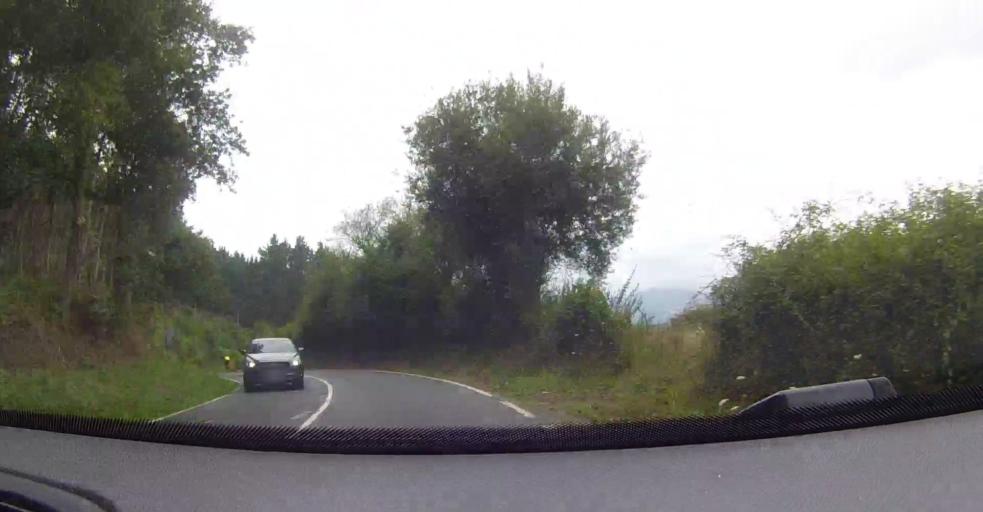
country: ES
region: Basque Country
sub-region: Bizkaia
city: Balmaseda
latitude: 43.2406
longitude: -3.2430
